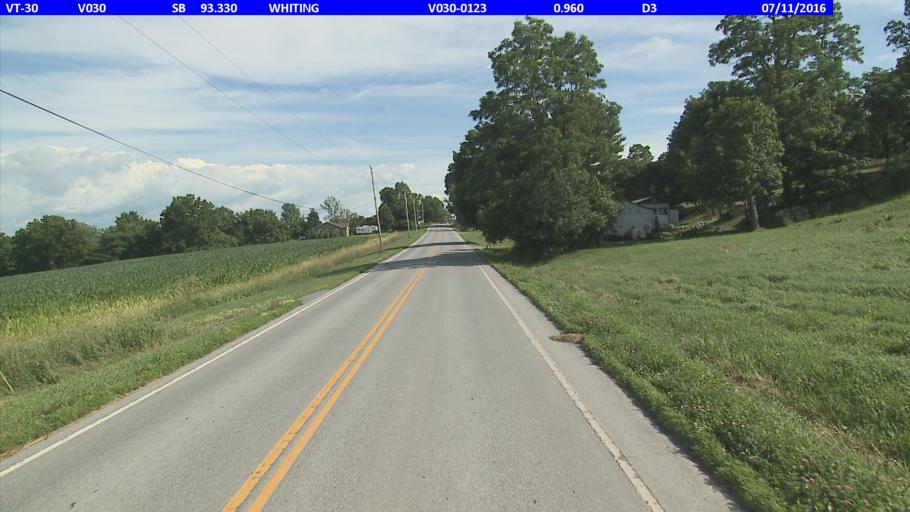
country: US
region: Vermont
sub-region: Rutland County
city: Brandon
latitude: 43.8516
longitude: -73.1997
